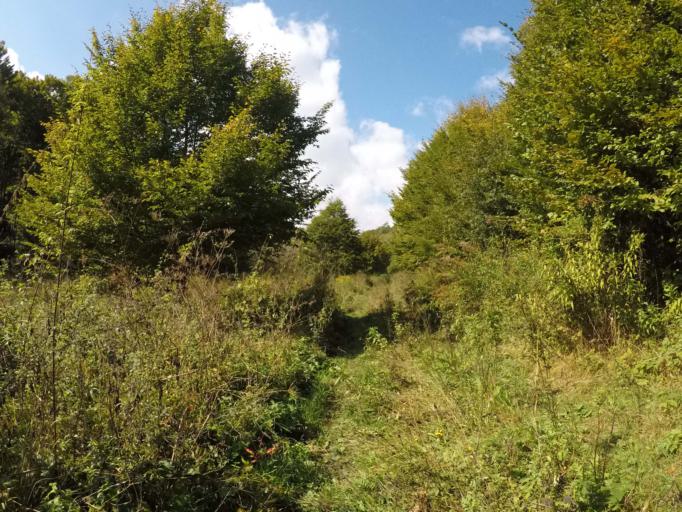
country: SK
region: Presovsky
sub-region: Okres Presov
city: Presov
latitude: 48.9355
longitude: 21.1576
